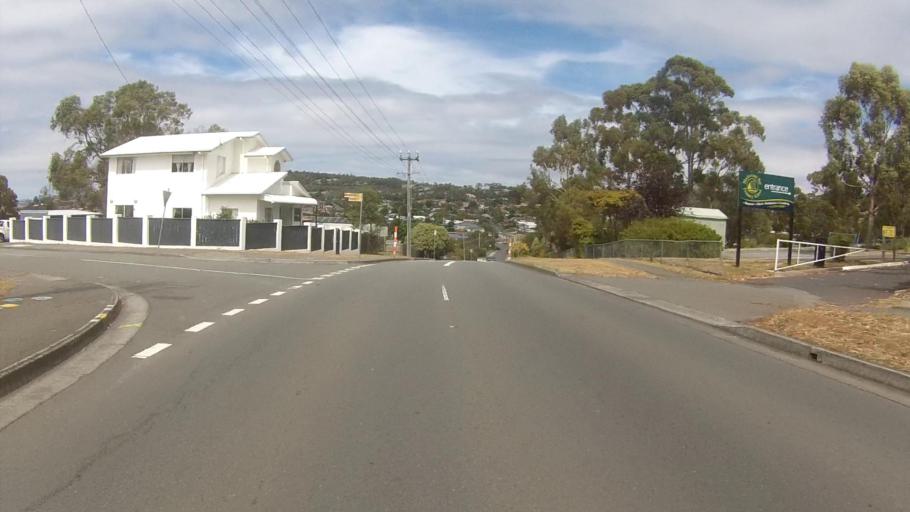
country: AU
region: Tasmania
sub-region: Kingborough
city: Blackmans Bay
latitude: -42.9966
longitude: 147.3230
